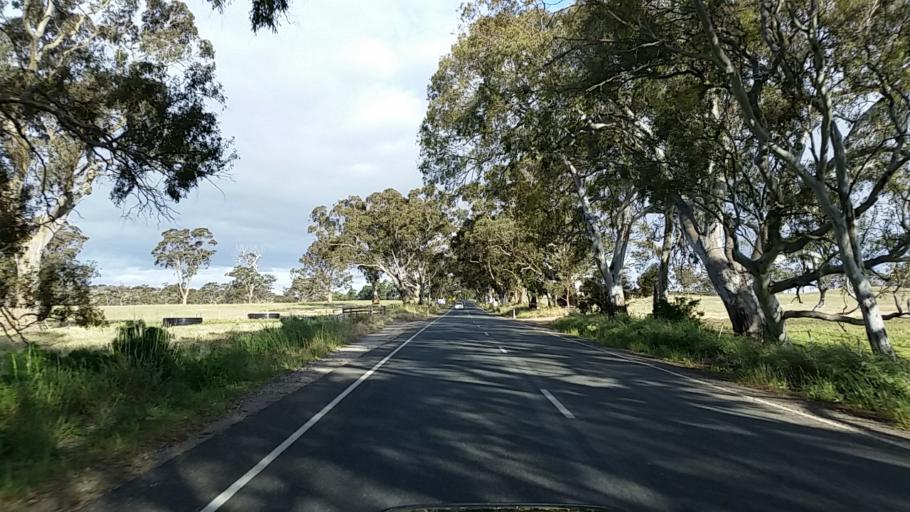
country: AU
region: South Australia
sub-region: Barossa
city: Angaston
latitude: -34.5566
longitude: 139.1405
